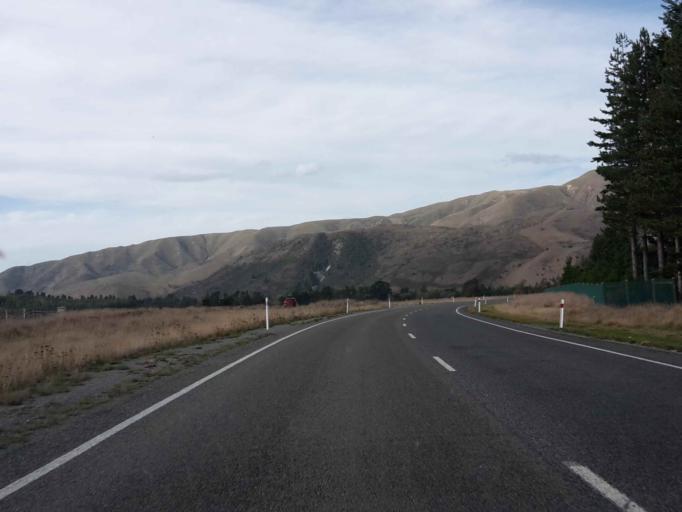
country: NZ
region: Canterbury
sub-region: Timaru District
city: Pleasant Point
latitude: -44.0893
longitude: 170.6364
